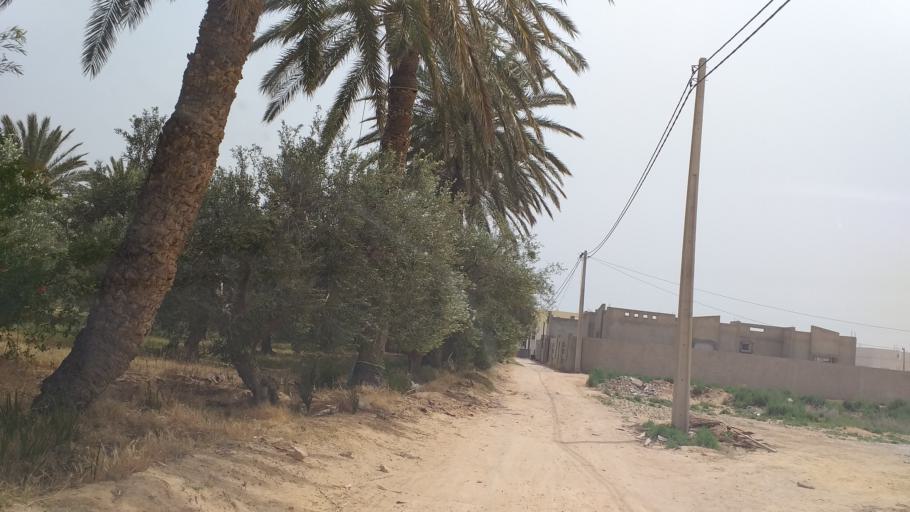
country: TN
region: Qabis
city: Gabes
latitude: 33.9517
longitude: 10.0644
